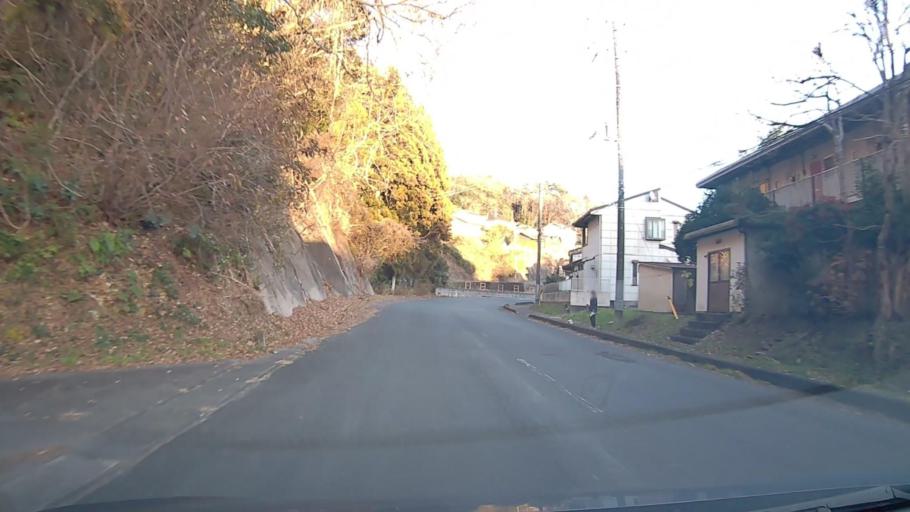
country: JP
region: Ibaraki
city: Kitaibaraki
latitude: 36.8551
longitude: 140.7824
